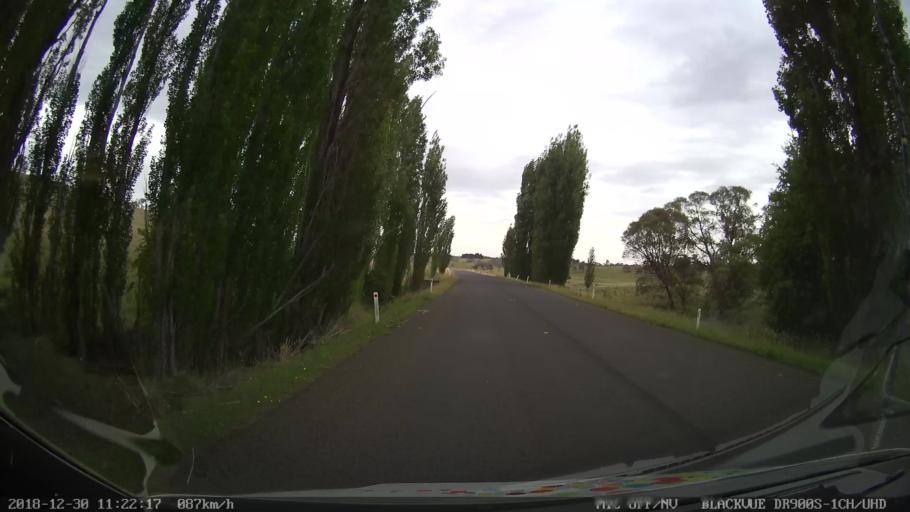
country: AU
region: New South Wales
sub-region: Snowy River
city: Jindabyne
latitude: -36.5017
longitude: 148.6707
